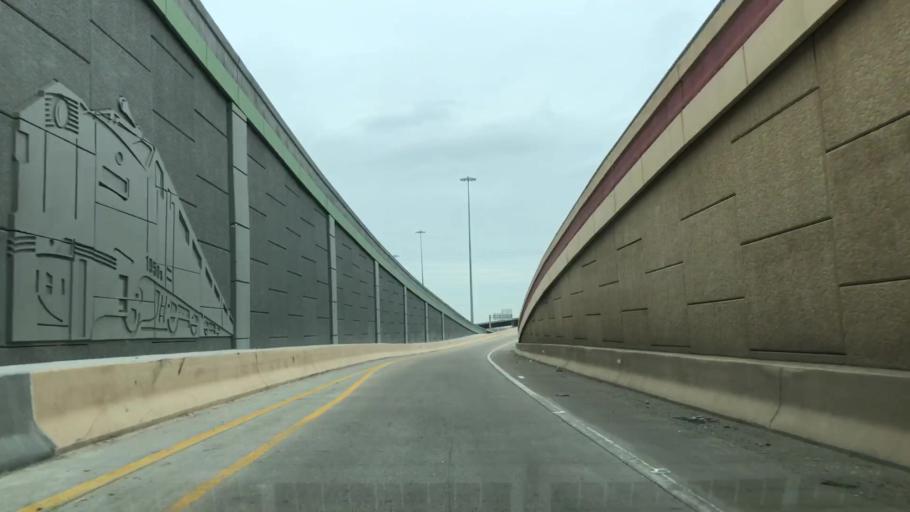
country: US
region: Texas
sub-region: Dallas County
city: Irving
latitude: 32.8416
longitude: -96.9141
